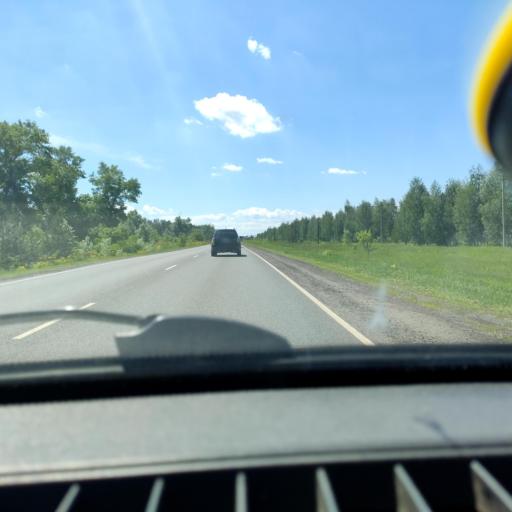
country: RU
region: Samara
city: Povolzhskiy
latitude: 53.5995
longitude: 49.5924
